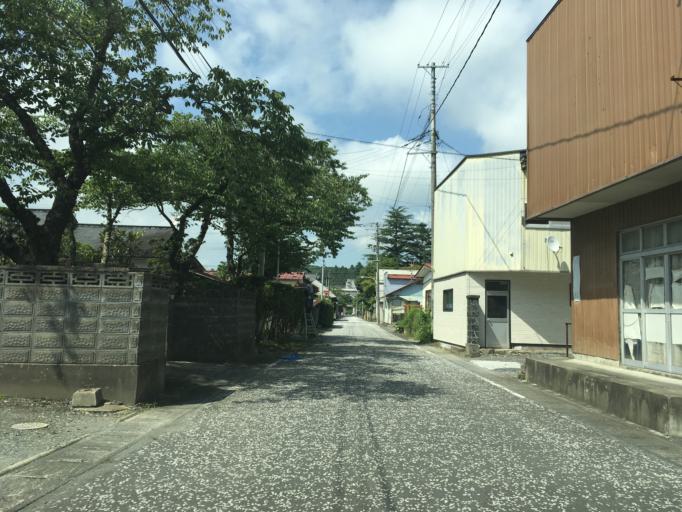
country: JP
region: Miyagi
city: Wakuya
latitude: 38.6529
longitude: 141.2788
